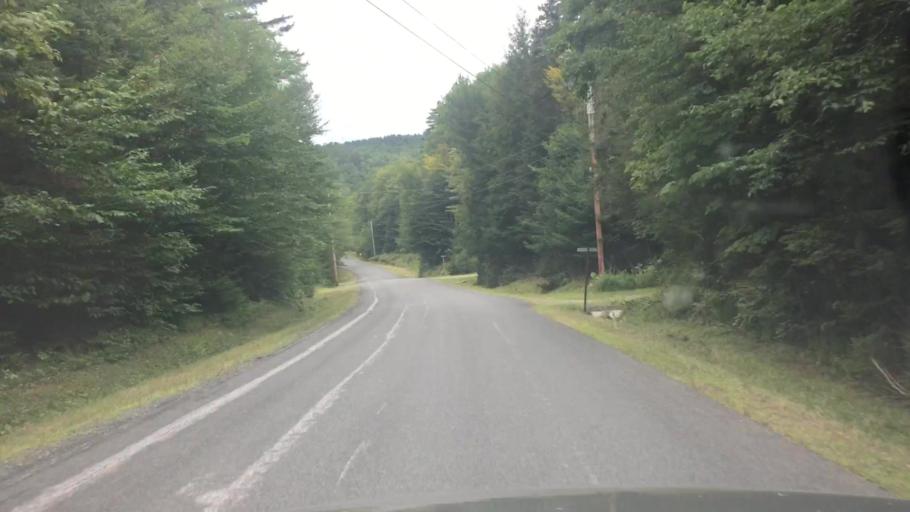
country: US
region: Vermont
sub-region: Windham County
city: Dover
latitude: 42.8465
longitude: -72.8320
